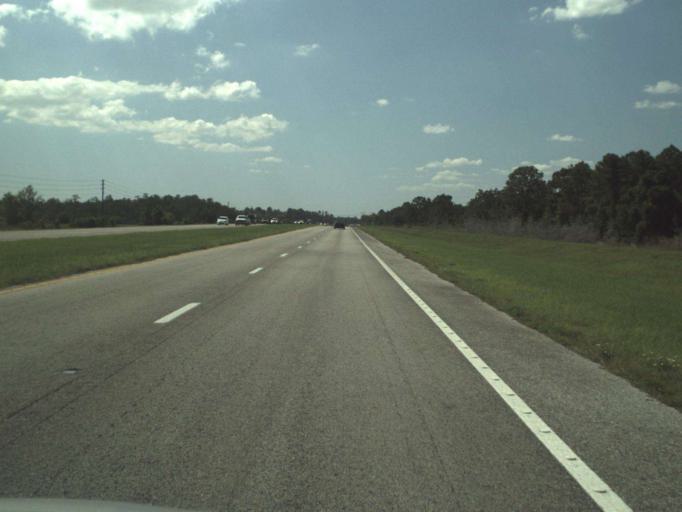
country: US
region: Florida
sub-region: Orange County
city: Wedgefield
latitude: 28.4824
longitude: -81.0296
